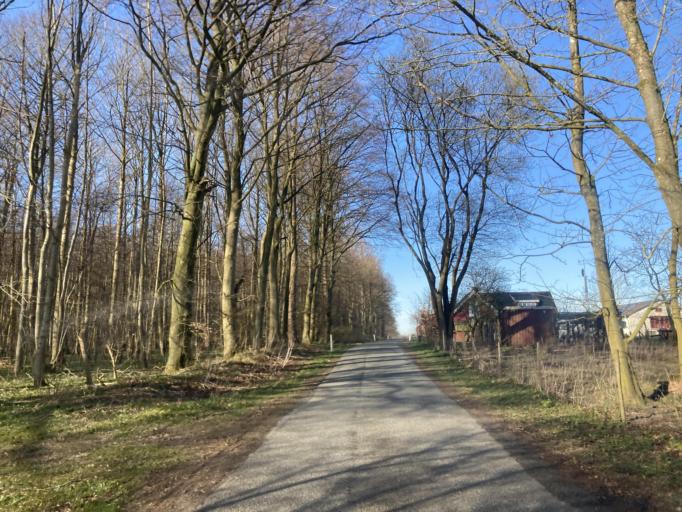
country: DK
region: Zealand
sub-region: Lejre Kommune
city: Kirke Hvalso
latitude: 55.5044
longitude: 11.8527
